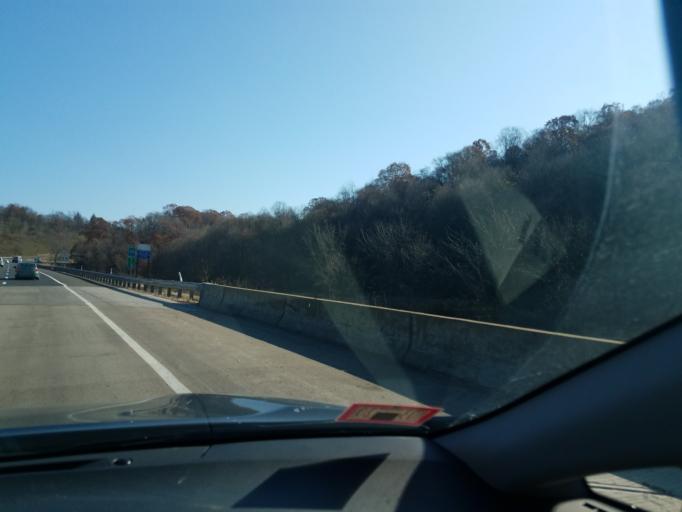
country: US
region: Pennsylvania
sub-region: Allegheny County
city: Avalon
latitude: 40.5198
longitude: -80.0612
